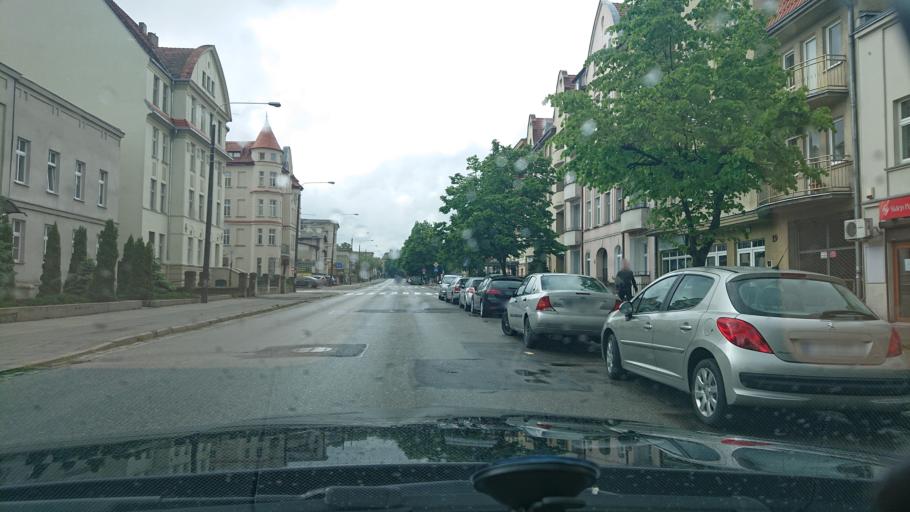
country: PL
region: Greater Poland Voivodeship
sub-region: Powiat gnieznienski
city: Gniezno
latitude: 52.5391
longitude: 17.6008
